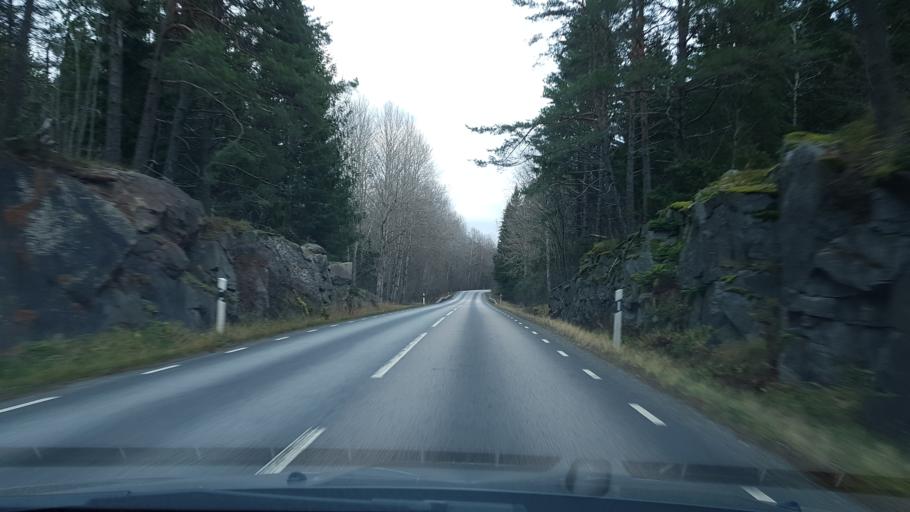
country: SE
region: Stockholm
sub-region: Norrtalje Kommun
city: Skanninge
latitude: 60.0274
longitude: 18.4165
